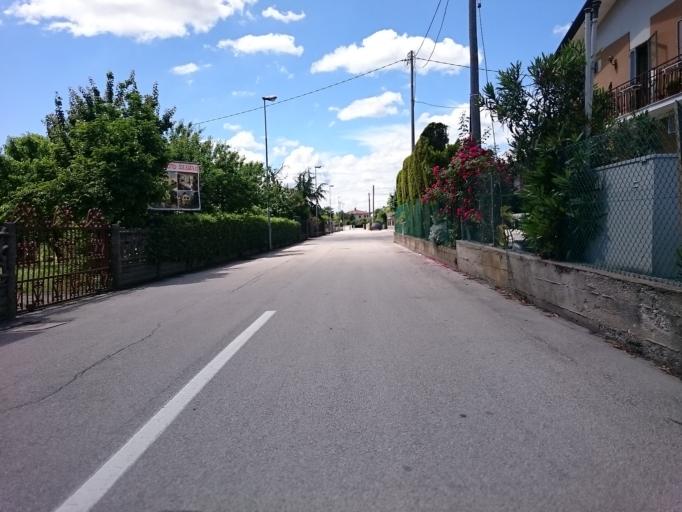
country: IT
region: Veneto
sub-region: Provincia di Padova
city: Campagnola
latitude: 45.2795
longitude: 11.9961
